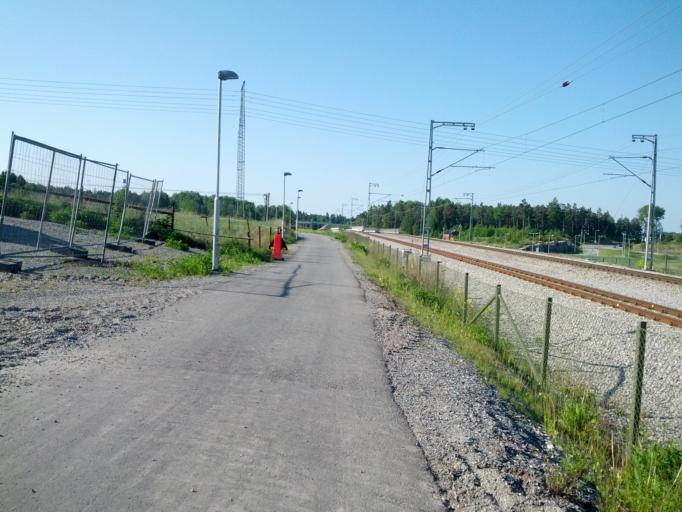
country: SE
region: Stockholm
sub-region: Taby Kommun
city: Taby
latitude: 59.4784
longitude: 18.0573
